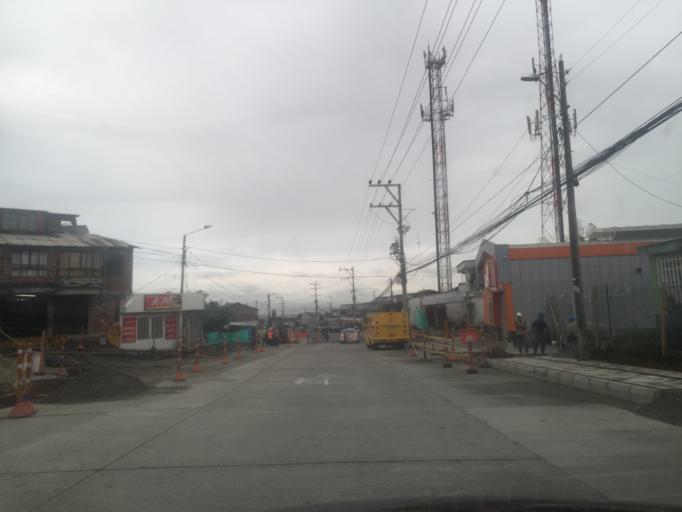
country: CO
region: Quindio
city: Armenia
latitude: 4.5197
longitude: -75.7056
